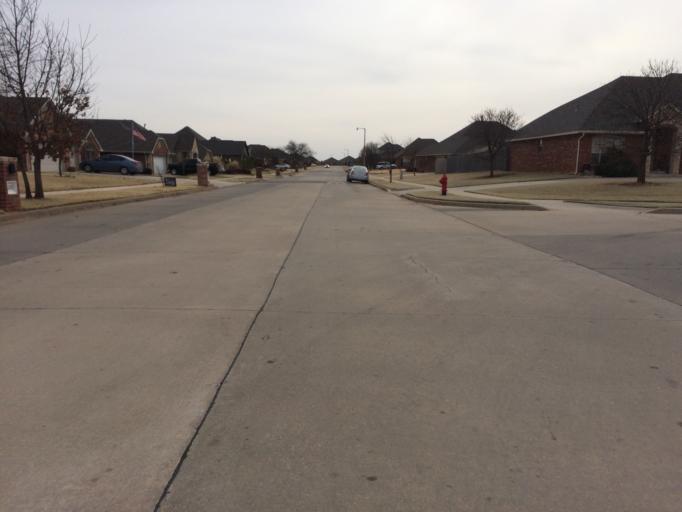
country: US
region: Oklahoma
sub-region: Cleveland County
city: Hall Park
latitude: 35.2153
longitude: -97.3960
